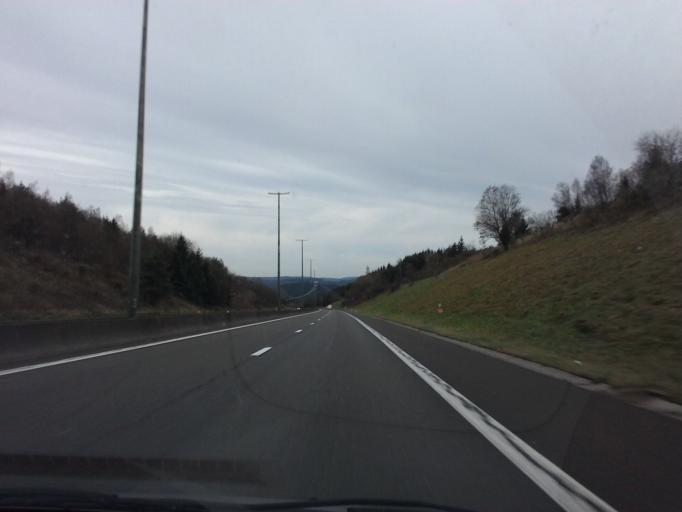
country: BE
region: Wallonia
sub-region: Province du Luxembourg
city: Manhay
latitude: 50.2785
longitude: 5.7280
